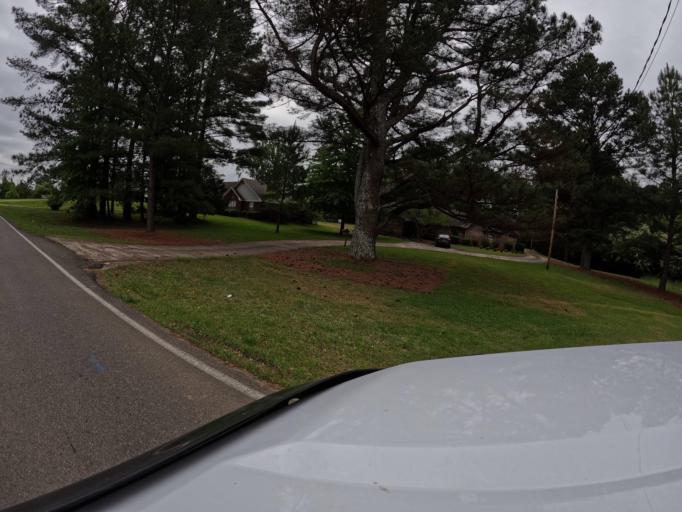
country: US
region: Mississippi
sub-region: Lee County
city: Tupelo
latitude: 34.2776
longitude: -88.7301
